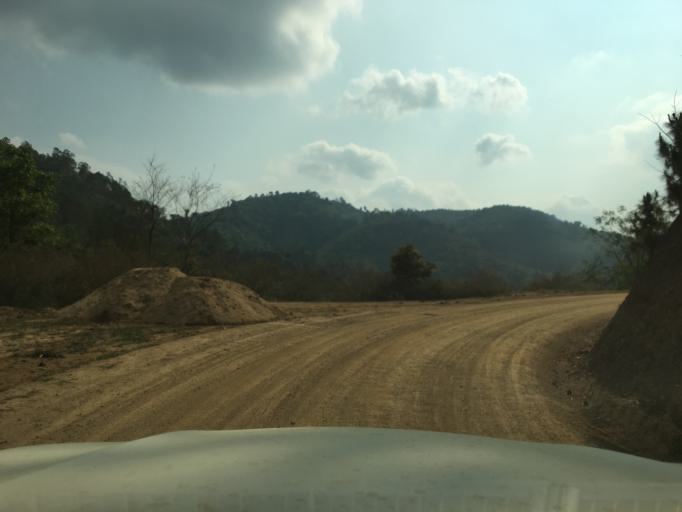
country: LA
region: Houaphan
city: Huameung
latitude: 20.2100
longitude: 103.8623
